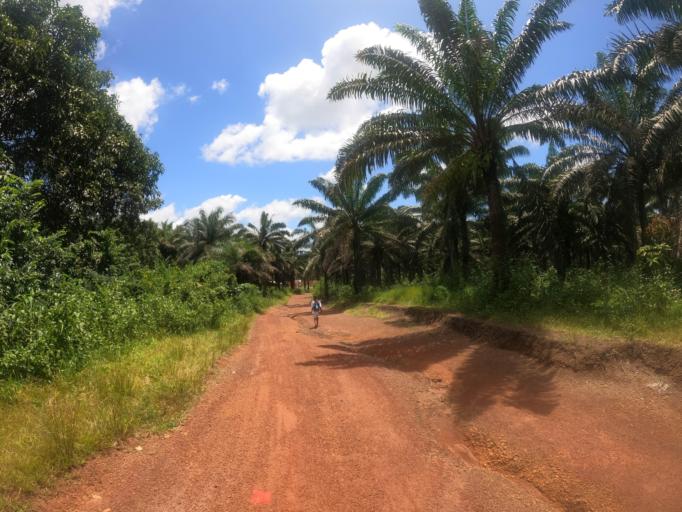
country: SL
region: Northern Province
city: Makeni
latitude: 8.8642
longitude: -12.1069
